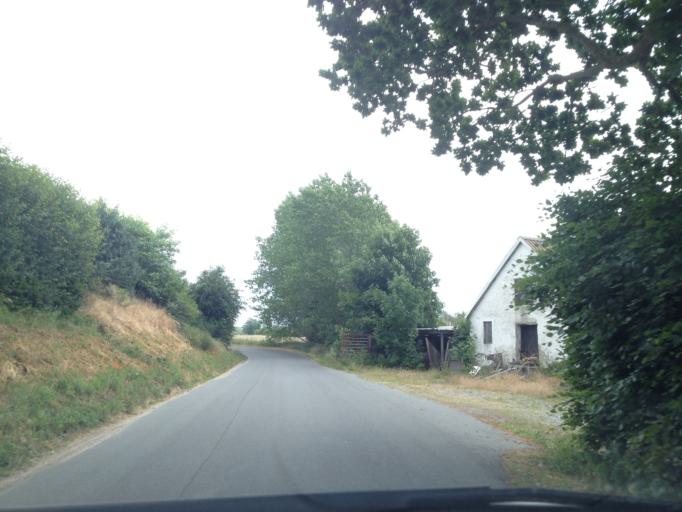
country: DK
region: Central Jutland
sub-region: Syddjurs Kommune
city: Ebeltoft
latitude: 56.1552
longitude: 10.6964
